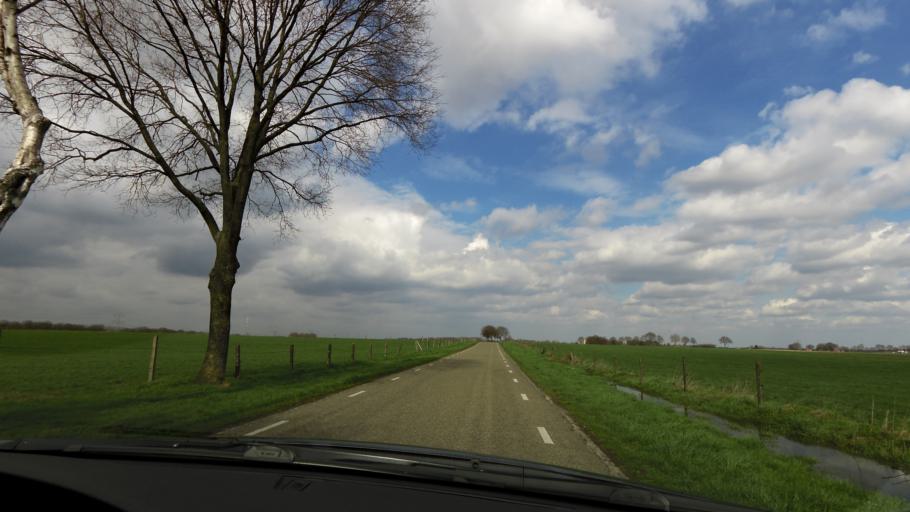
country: NL
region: Limburg
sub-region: Gemeente Sittard-Geleen
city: Limbricht
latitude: 51.0024
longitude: 5.8105
